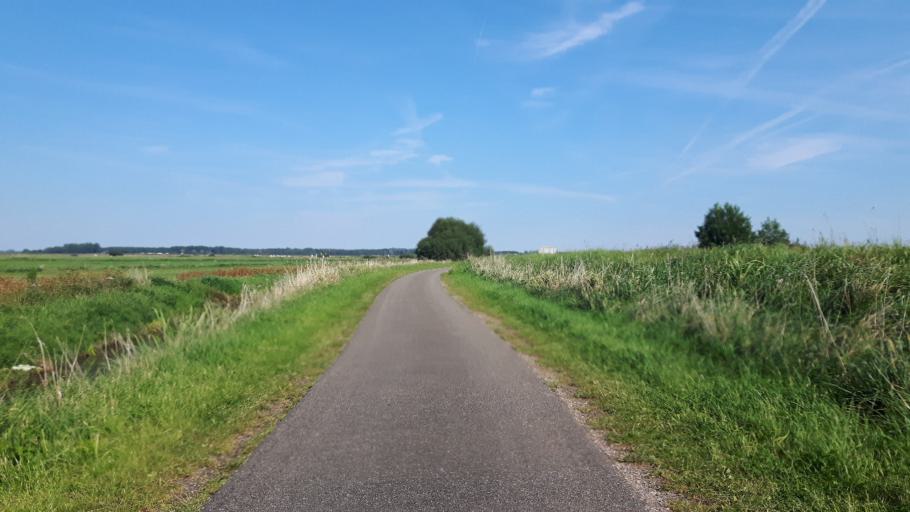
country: NL
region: Drenthe
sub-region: Gemeente Tynaarlo
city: Zuidlaren
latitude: 53.1300
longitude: 6.6769
